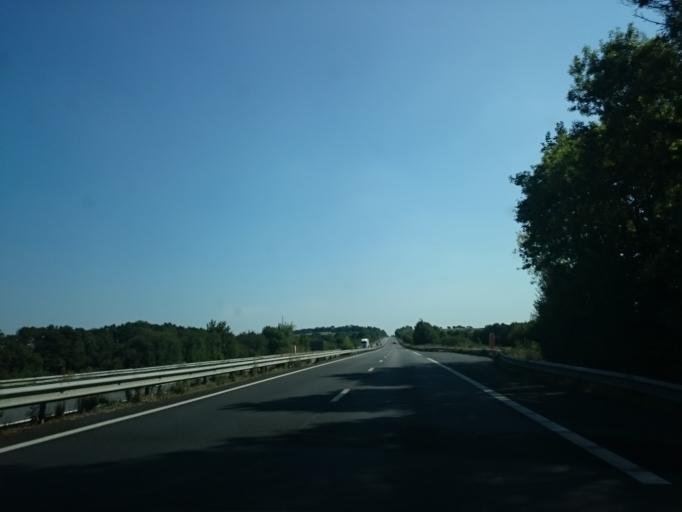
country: FR
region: Pays de la Loire
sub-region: Departement de la Loire-Atlantique
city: Derval
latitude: 47.6866
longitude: -1.6994
